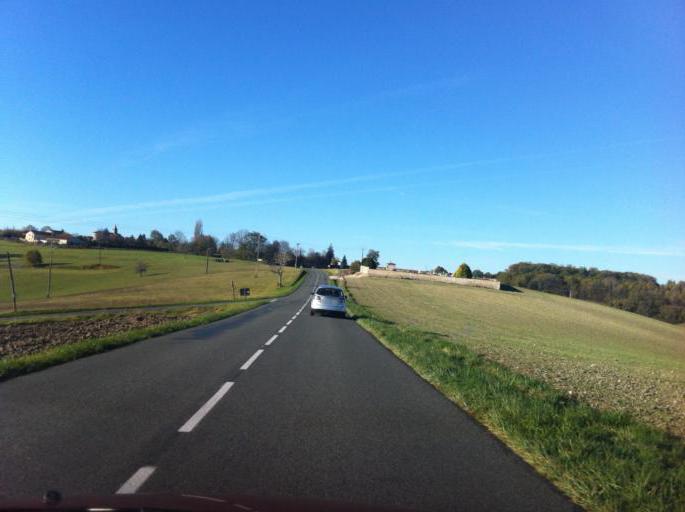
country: FR
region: Aquitaine
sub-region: Departement de la Dordogne
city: Saint-Aulaye
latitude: 45.2682
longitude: 0.1813
